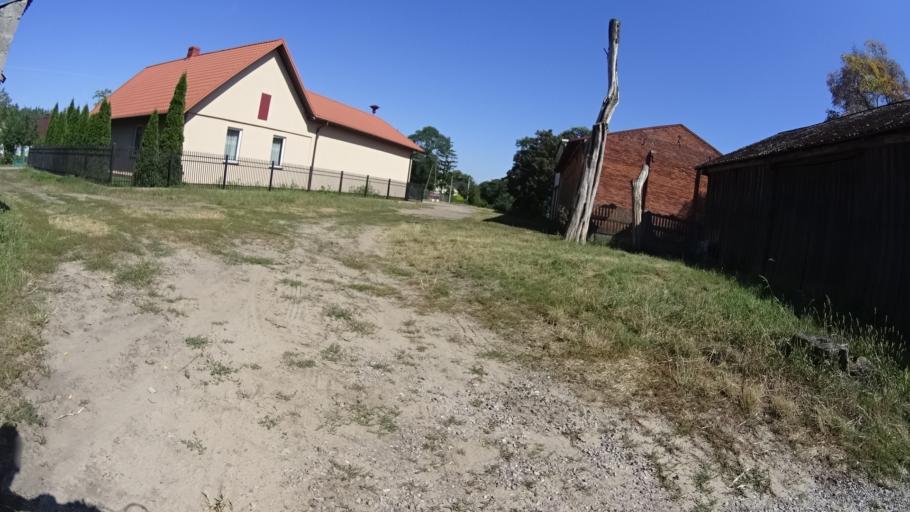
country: PL
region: Masovian Voivodeship
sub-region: Powiat bialobrzeski
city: Bialobrzegi
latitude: 51.6690
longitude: 20.9125
